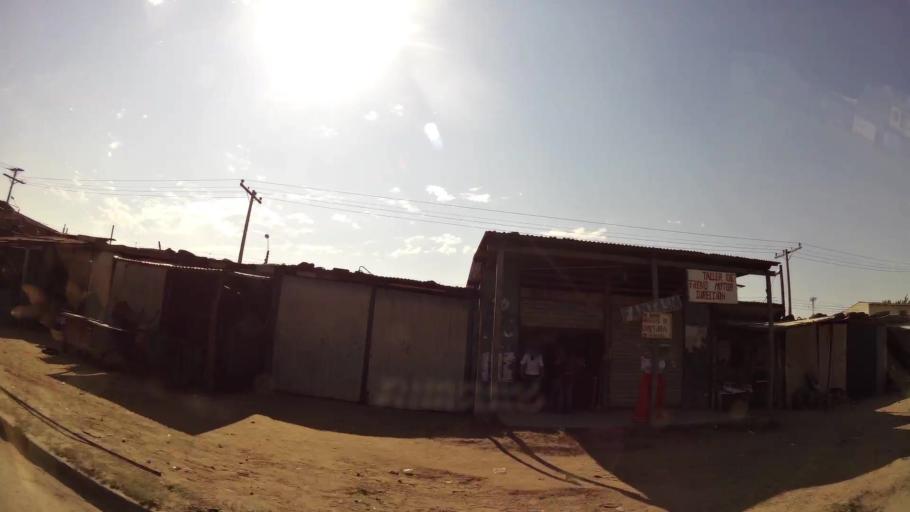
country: BO
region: Santa Cruz
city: Santa Cruz de la Sierra
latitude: -17.8239
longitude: -63.1297
